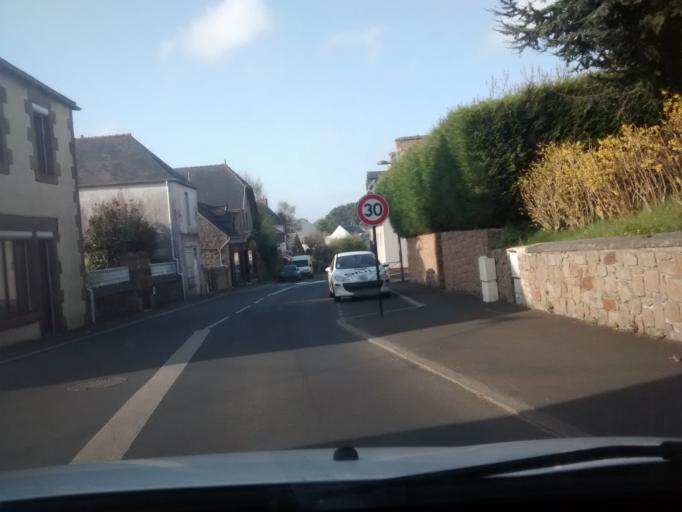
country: FR
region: Brittany
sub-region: Departement des Cotes-d'Armor
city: Perros-Guirec
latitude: 48.8095
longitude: -3.4403
